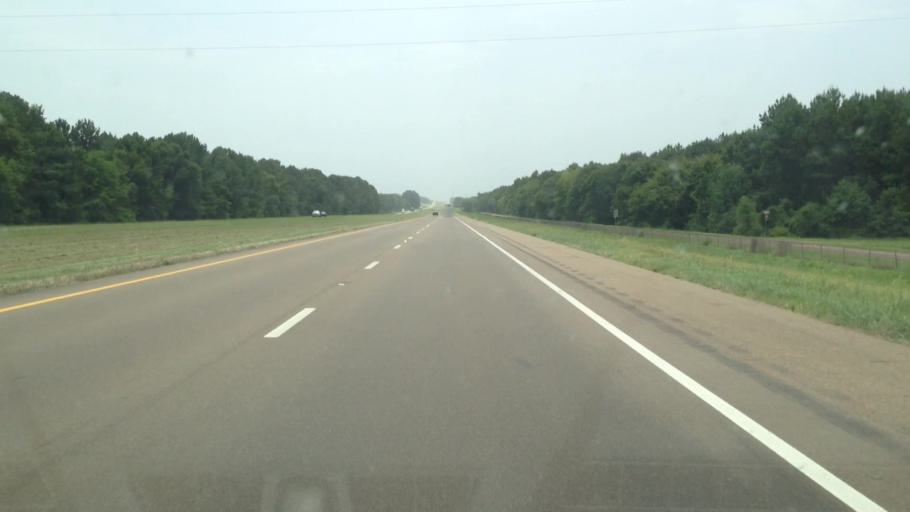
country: US
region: Texas
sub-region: Bowie County
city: De Kalb
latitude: 33.4336
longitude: -94.5340
